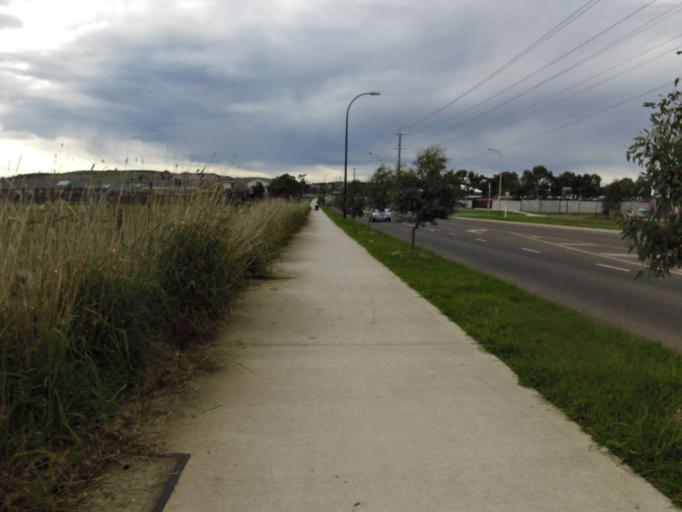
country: AU
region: Victoria
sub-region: Whittlesea
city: Epping
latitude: -37.6236
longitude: 145.0346
